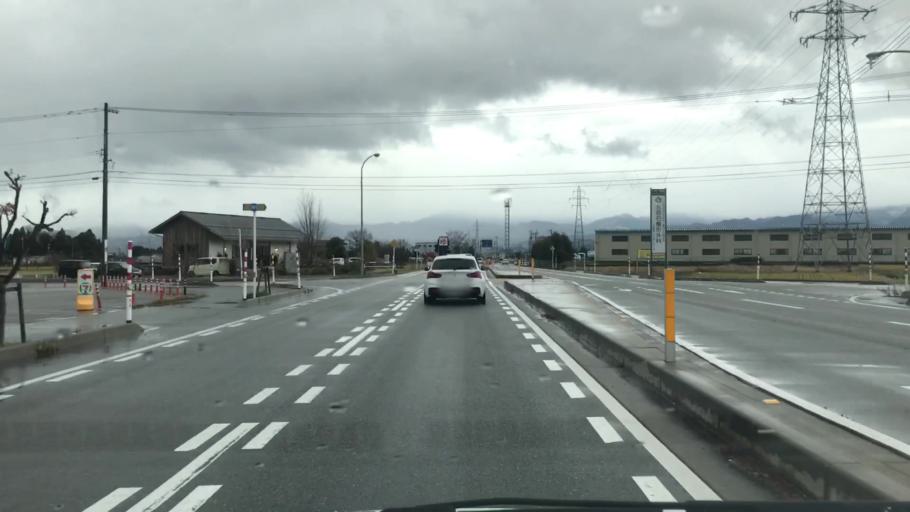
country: JP
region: Toyama
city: Kamiichi
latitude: 36.6865
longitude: 137.2996
